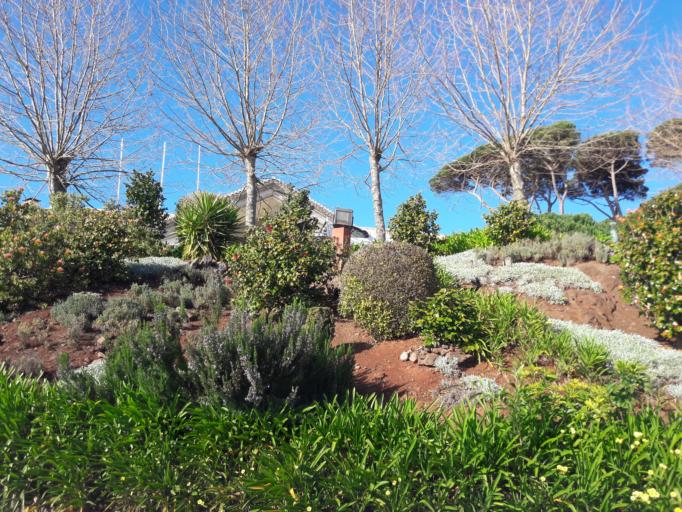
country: PT
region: Madeira
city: Canico
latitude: 32.6528
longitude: -16.8722
